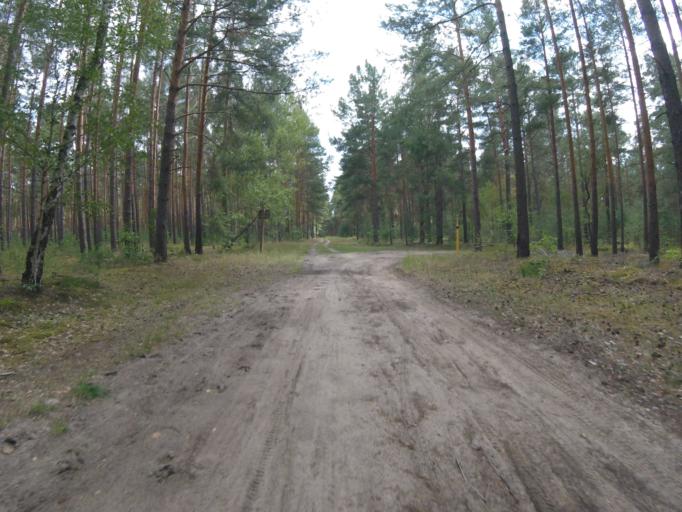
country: DE
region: Brandenburg
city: Halbe
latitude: 52.1335
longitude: 13.6956
